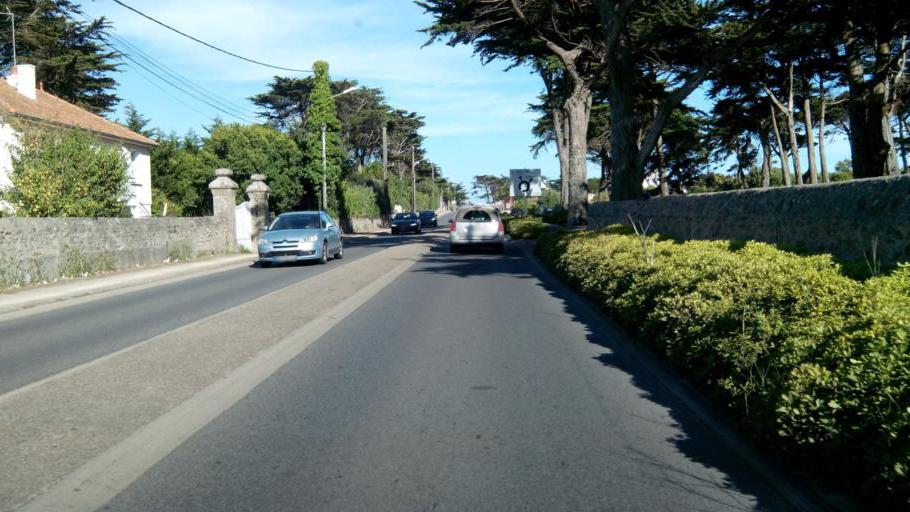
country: FR
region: Pays de la Loire
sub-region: Departement de la Loire-Atlantique
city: Le Croisic
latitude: 47.2818
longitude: -2.4999
